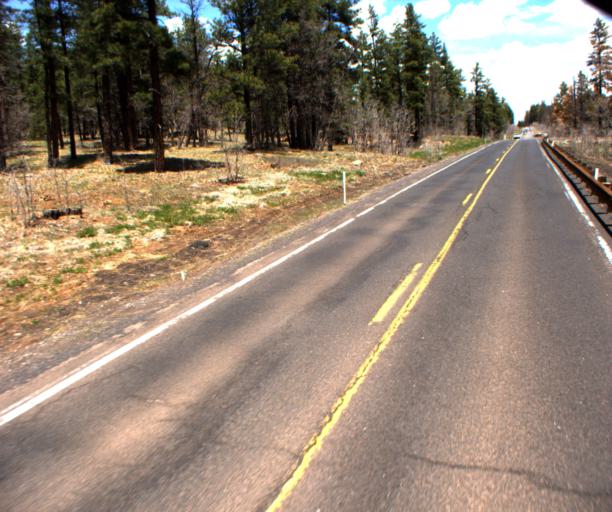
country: US
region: Arizona
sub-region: Coconino County
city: Kachina Village
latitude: 35.0523
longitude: -111.7328
